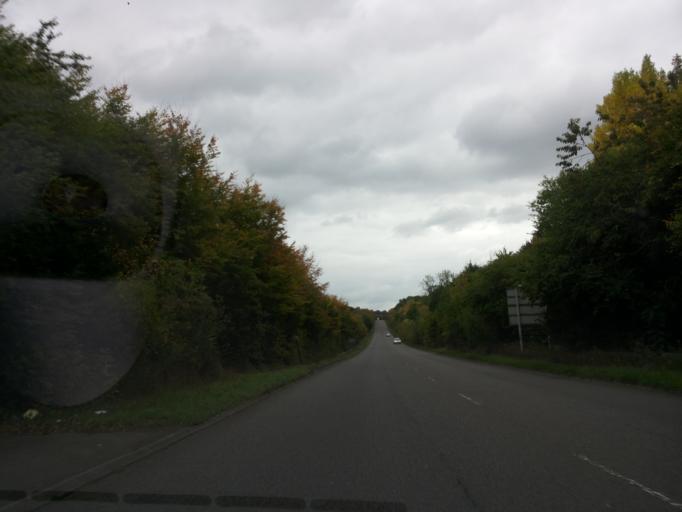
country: GB
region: England
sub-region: Buckinghamshire
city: Amersham
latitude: 51.6721
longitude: -0.6309
